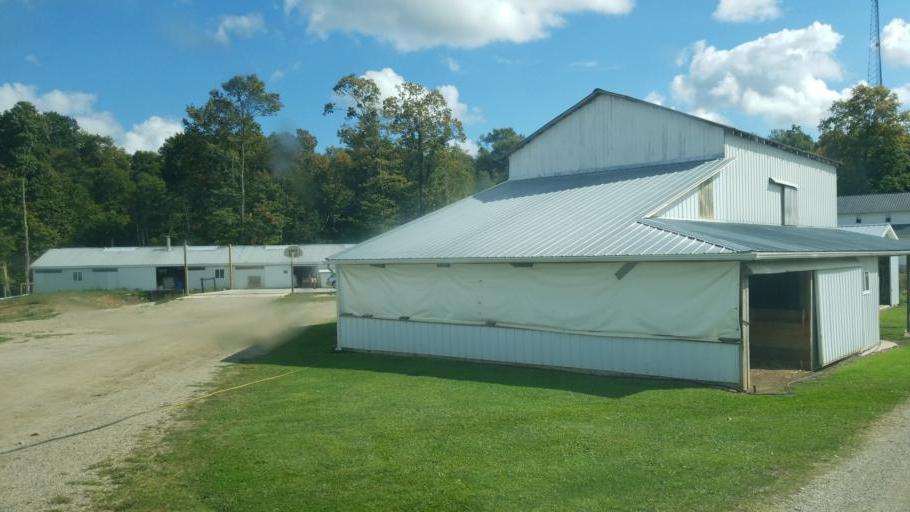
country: US
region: Ohio
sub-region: Knox County
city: Fredericktown
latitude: 40.5448
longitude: -82.6614
